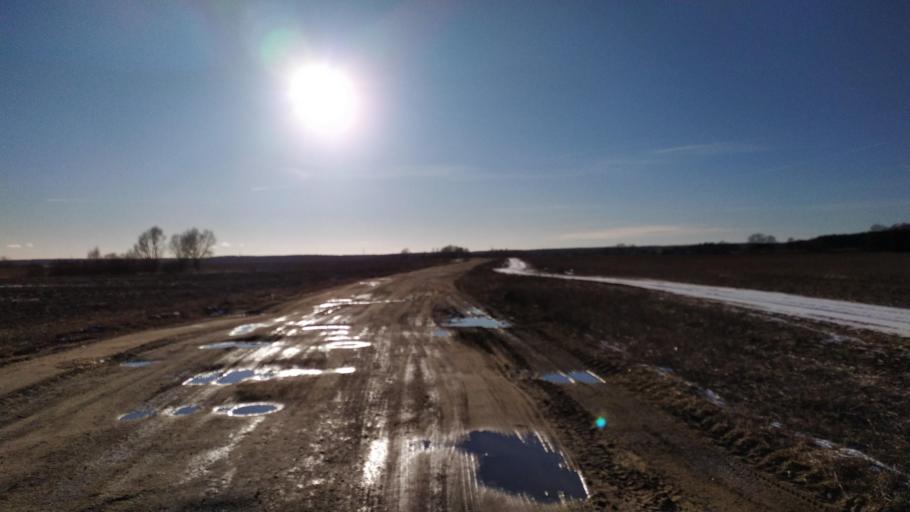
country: BY
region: Brest
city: Kamyanyets
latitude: 52.3712
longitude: 23.8918
